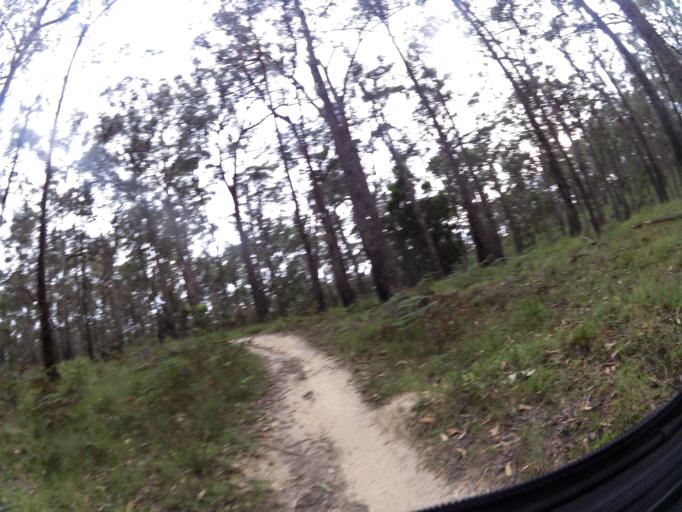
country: AU
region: Victoria
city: Brown Hill
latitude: -37.5240
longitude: 143.9068
